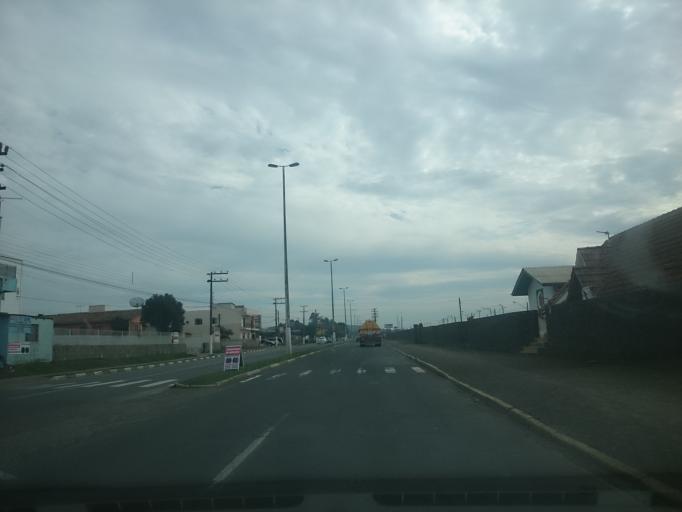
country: BR
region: Santa Catarina
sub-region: Lages
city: Lages
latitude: -27.7893
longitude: -50.3075
